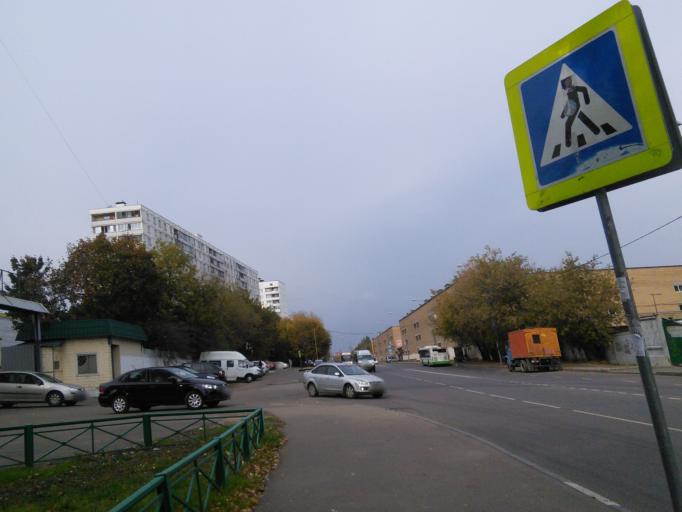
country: RU
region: Moskovskaya
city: Levoberezhnaya
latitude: 55.8693
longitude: 37.4729
